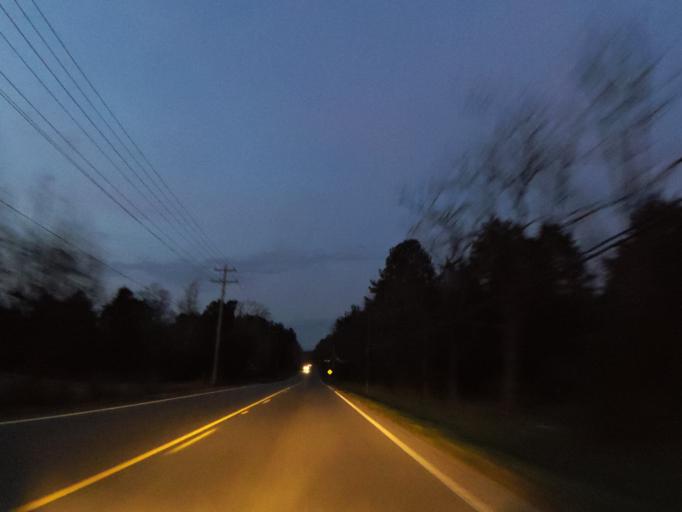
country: US
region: Tennessee
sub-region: Polk County
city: Benton
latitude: 35.0993
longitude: -84.7281
